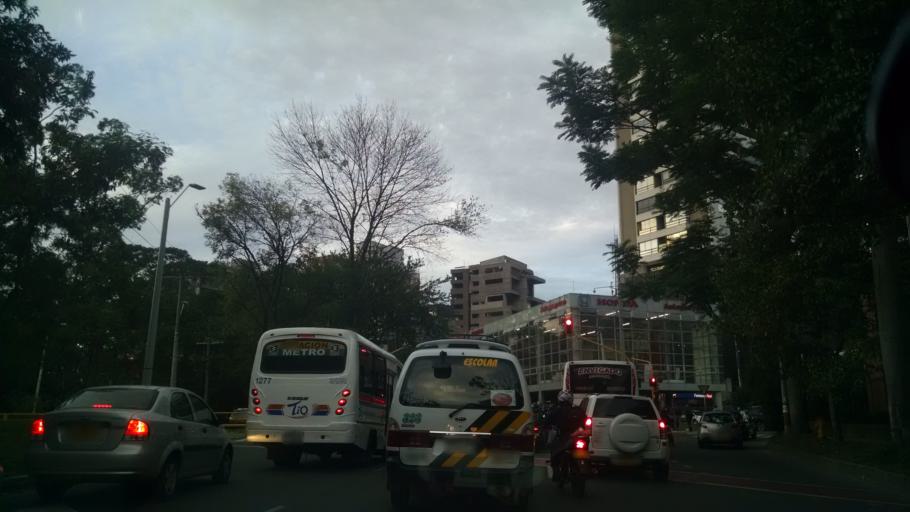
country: CO
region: Antioquia
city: Envigado
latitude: 6.1811
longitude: -75.5812
